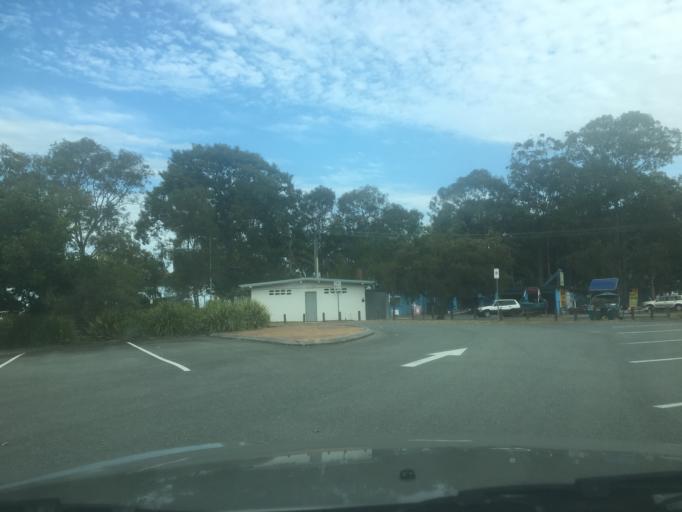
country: AU
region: Queensland
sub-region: Moreton Bay
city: Bongaree
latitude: -27.0679
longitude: 153.1335
